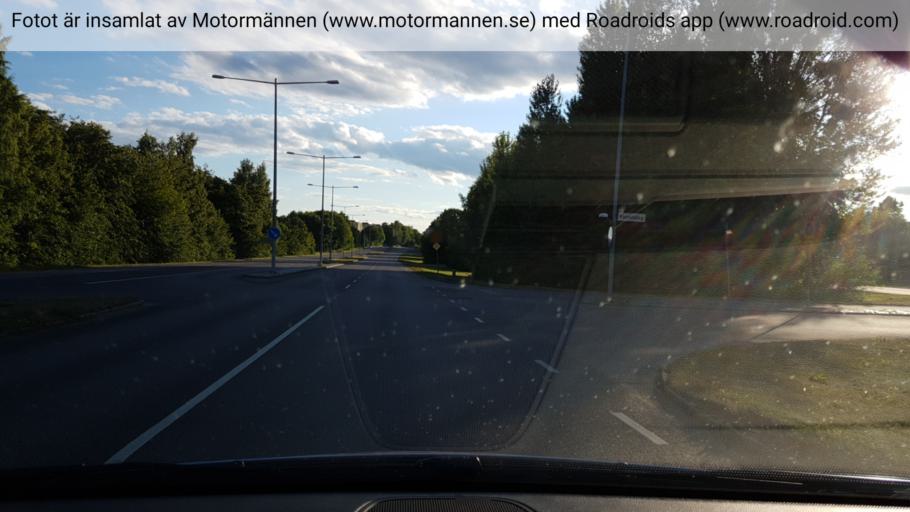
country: SE
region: Vaestmanland
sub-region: Vasteras
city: Hokasen
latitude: 59.6237
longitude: 16.6082
